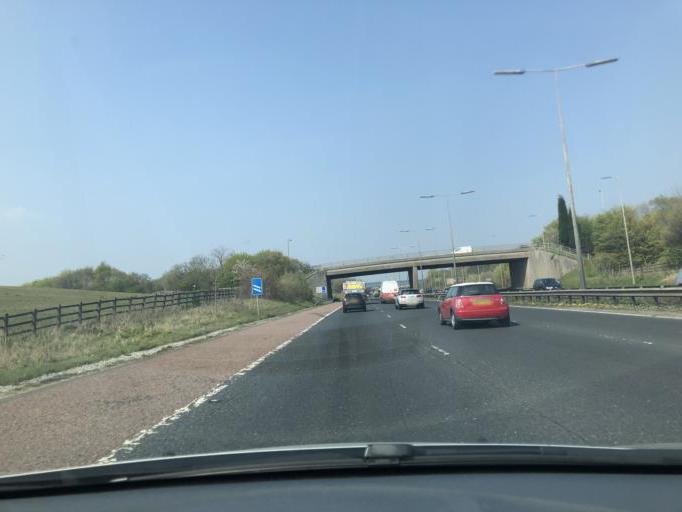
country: GB
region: England
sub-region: Borough of Tameside
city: Denton
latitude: 53.4486
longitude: -2.1350
